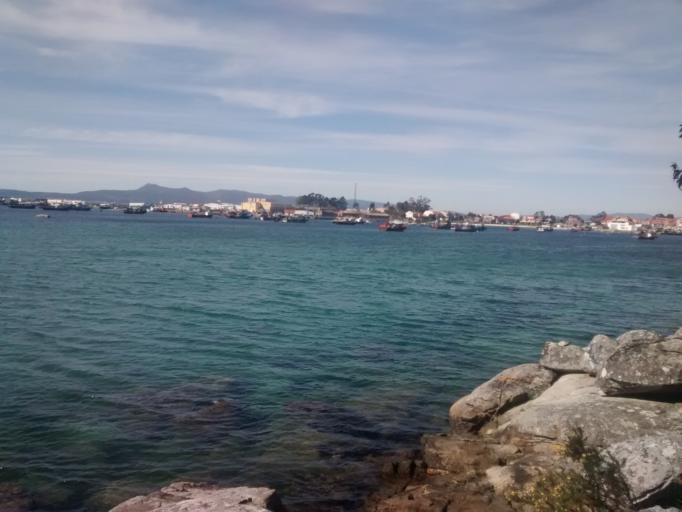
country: ES
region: Galicia
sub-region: Provincia de Pontevedra
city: O Grove
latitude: 42.4854
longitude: -8.8869
